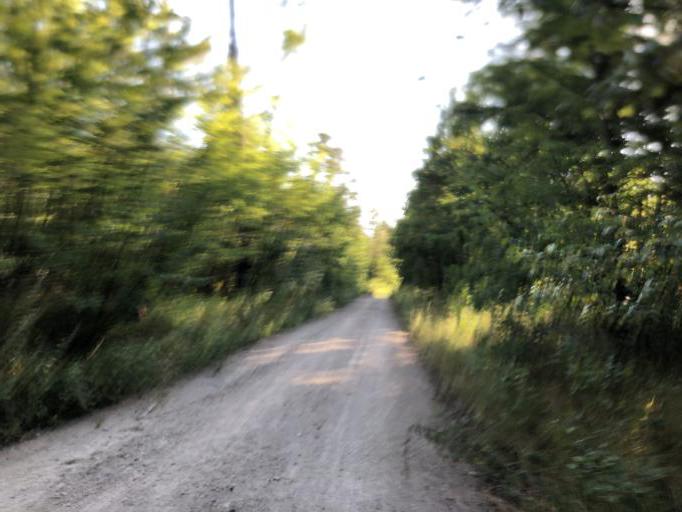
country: DE
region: Bavaria
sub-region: Regierungsbezirk Mittelfranken
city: Buckenhof
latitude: 49.5401
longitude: 11.0409
